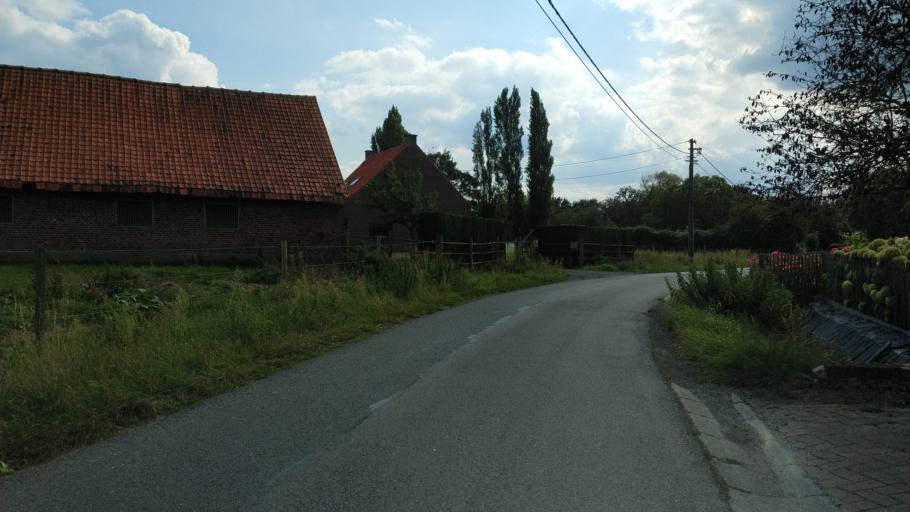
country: BE
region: Flanders
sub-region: Provincie Oost-Vlaanderen
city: Evergem
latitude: 51.1147
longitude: 3.6706
